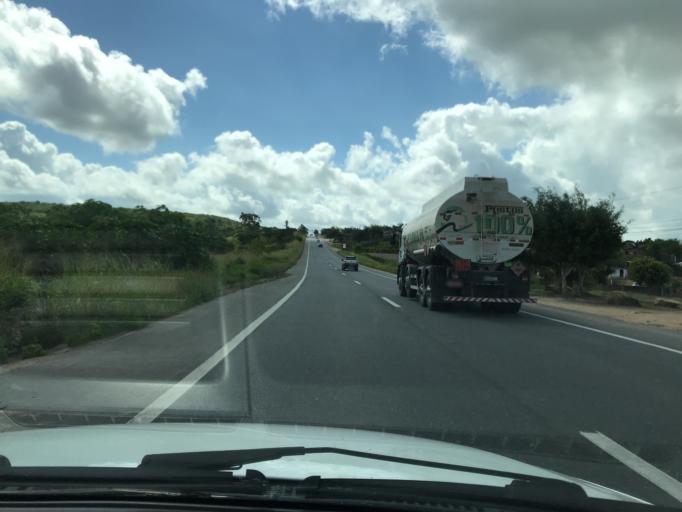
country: BR
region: Pernambuco
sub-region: Cha Grande
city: Cha Grande
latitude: -8.1836
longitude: -35.4924
